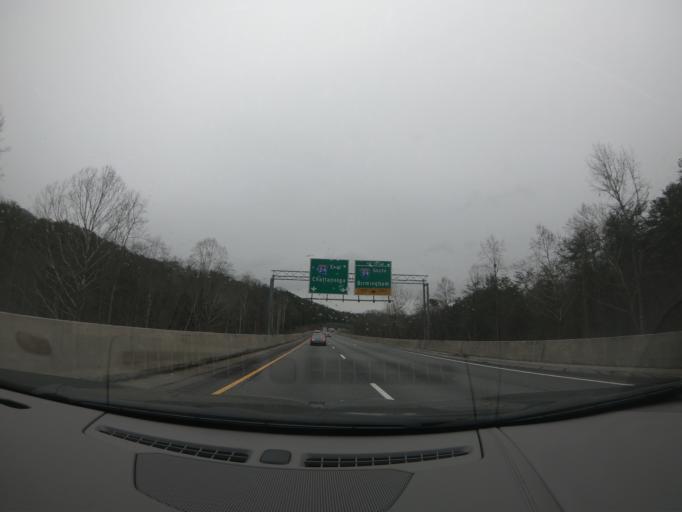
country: US
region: Georgia
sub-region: Walker County
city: Lookout Mountain
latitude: 34.9814
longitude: -85.4630
